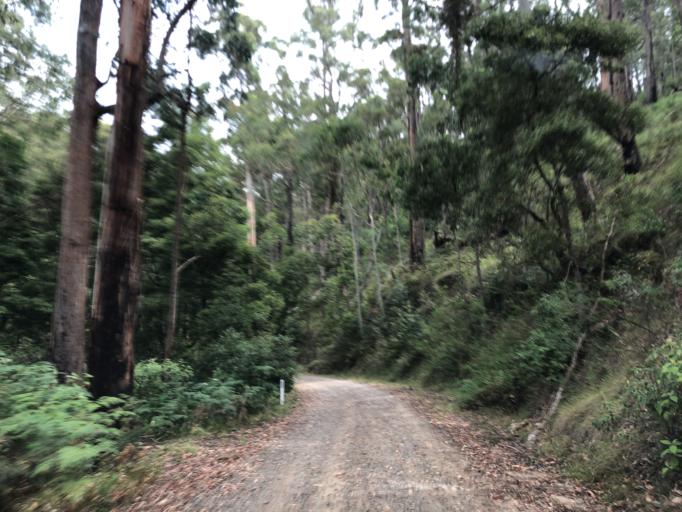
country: AU
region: Victoria
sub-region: Moorabool
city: Bacchus Marsh
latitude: -37.4562
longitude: 144.2687
